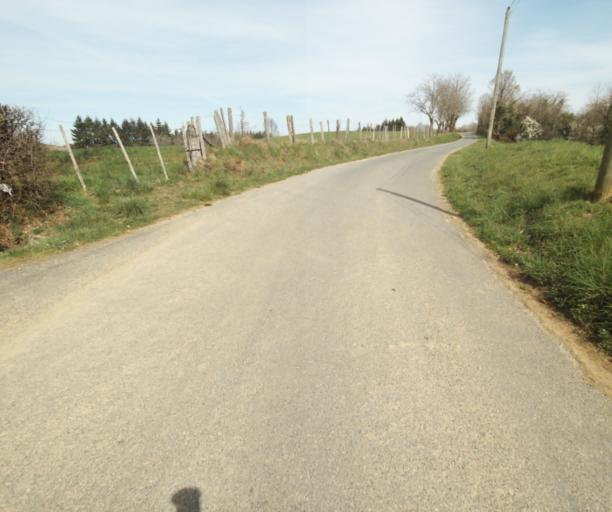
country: FR
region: Limousin
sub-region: Departement de la Correze
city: Naves
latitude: 45.3394
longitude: 1.7682
